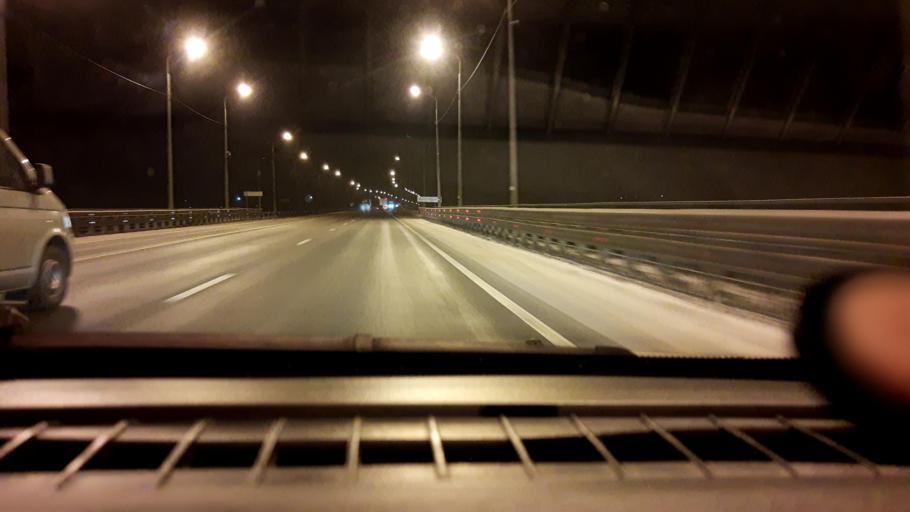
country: RU
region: Nizjnij Novgorod
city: Vorotynets
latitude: 56.0514
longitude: 45.8462
